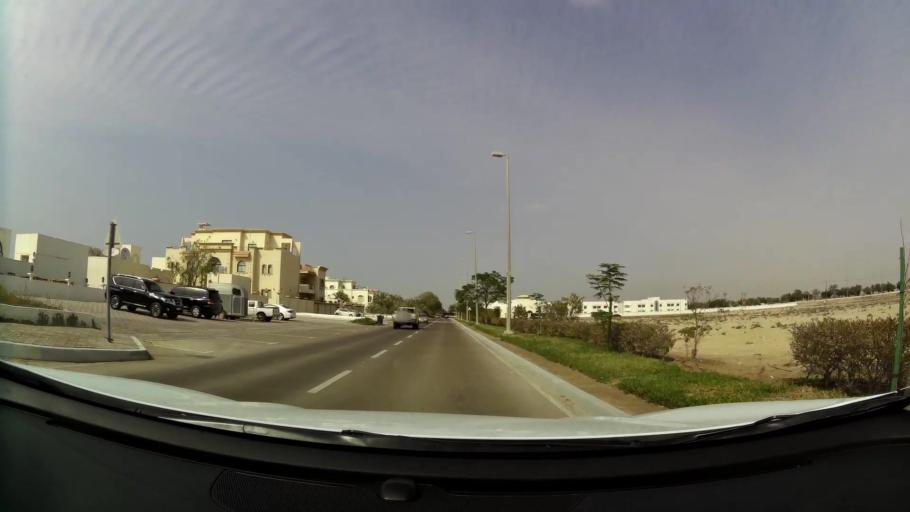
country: AE
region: Abu Dhabi
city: Abu Dhabi
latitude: 24.5675
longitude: 54.6929
